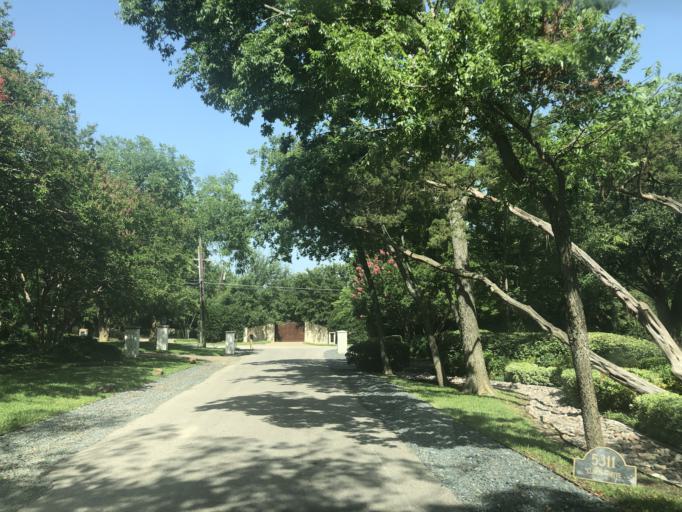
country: US
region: Texas
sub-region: Dallas County
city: University Park
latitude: 32.8787
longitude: -96.8162
